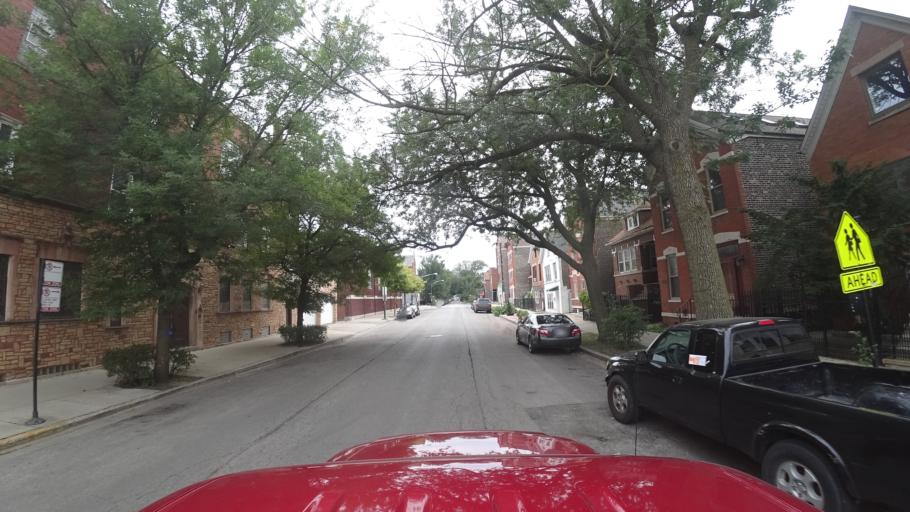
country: US
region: Illinois
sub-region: Cook County
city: Chicago
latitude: 41.8361
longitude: -87.6536
